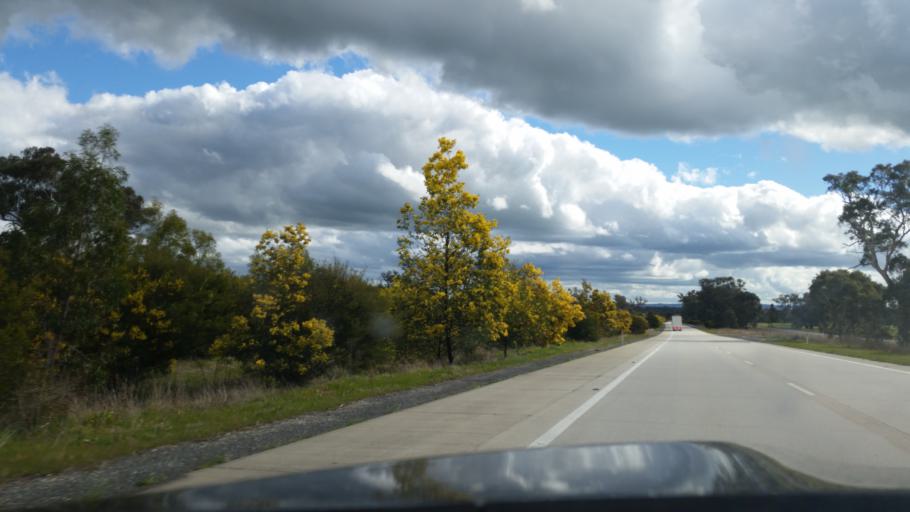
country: AU
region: New South Wales
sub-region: Greater Hume Shire
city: Jindera
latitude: -35.9247
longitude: 147.0449
